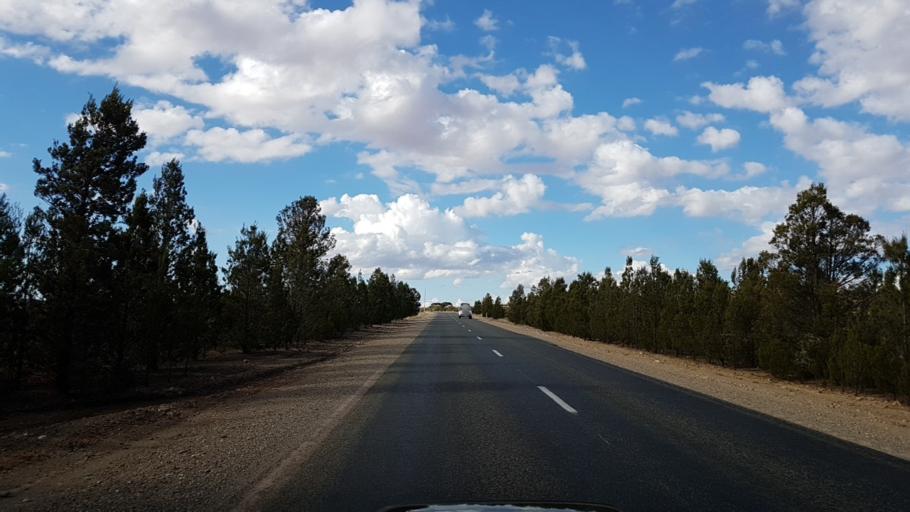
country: AU
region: South Australia
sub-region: Peterborough
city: Peterborough
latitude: -32.9623
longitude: 138.8862
